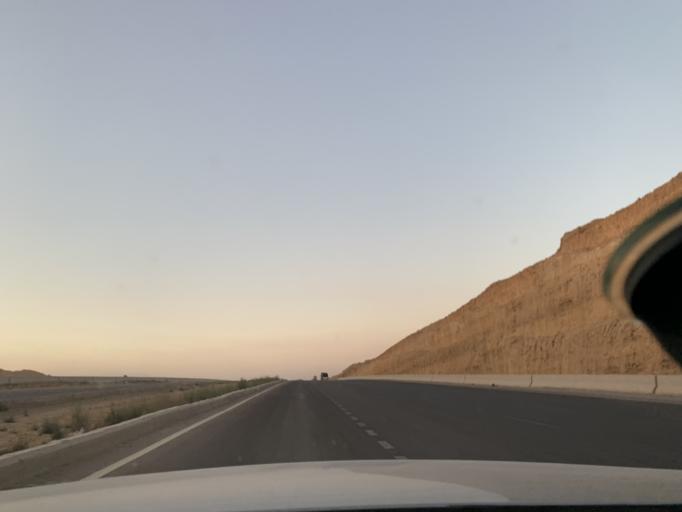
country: EG
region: Muhafazat al Qahirah
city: Halwan
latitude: 29.9509
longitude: 31.5388
